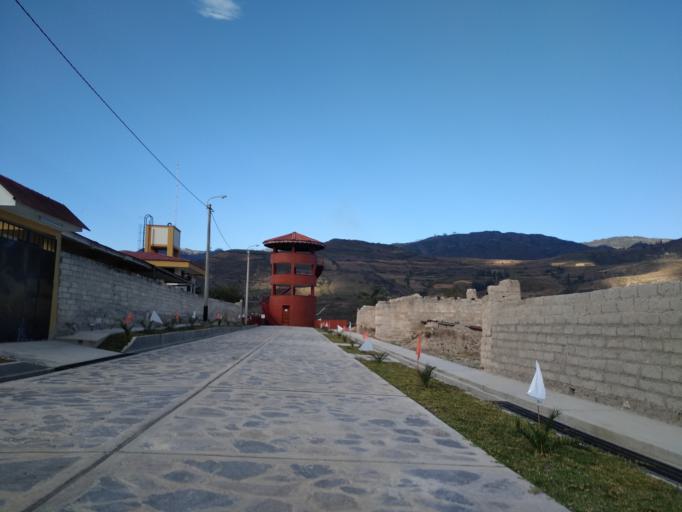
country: PE
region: Amazonas
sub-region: Provincia de Luya
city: Tingo
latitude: -6.3719
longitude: -77.9091
